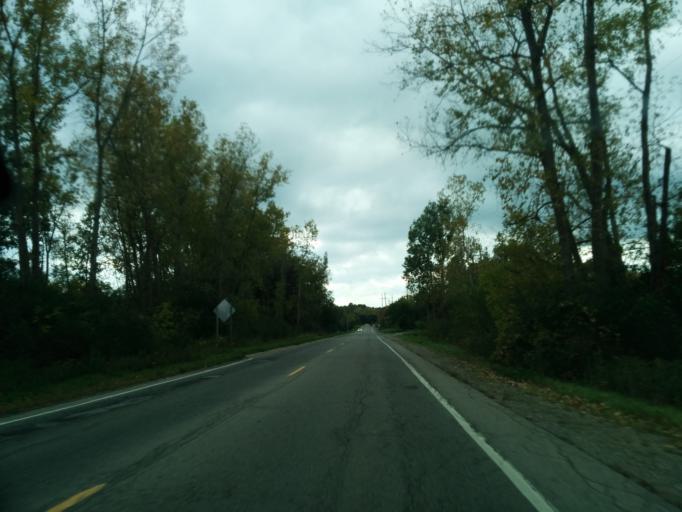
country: US
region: Michigan
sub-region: Oakland County
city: Waterford
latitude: 42.7001
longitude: -83.4591
